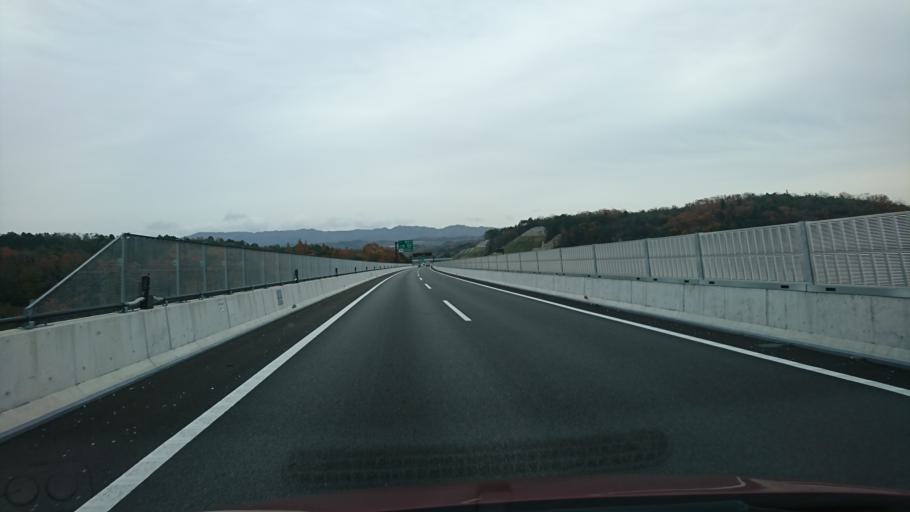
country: JP
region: Hyogo
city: Kawanishi
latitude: 34.8887
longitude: 135.3847
